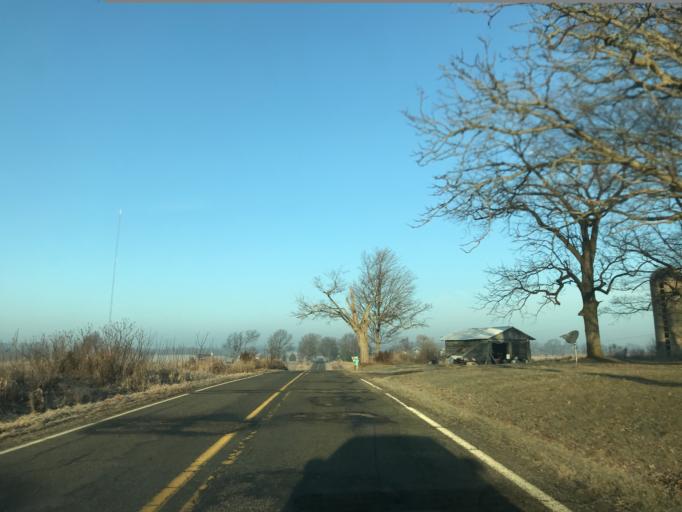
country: US
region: Michigan
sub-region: Ingham County
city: Leslie
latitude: 42.4169
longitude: -84.5086
